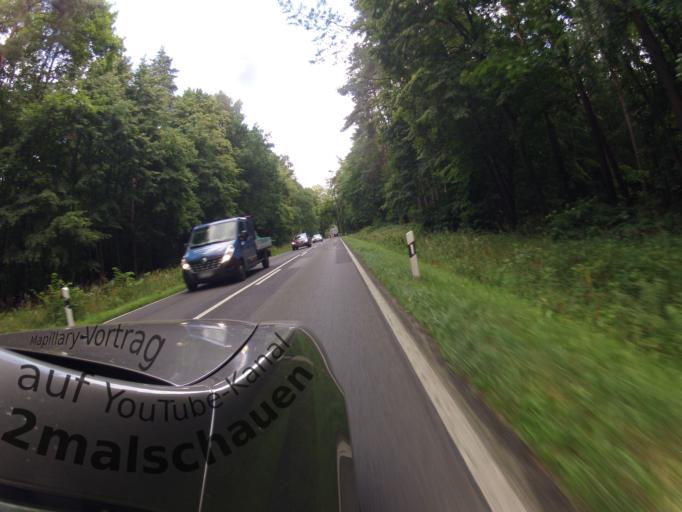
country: DE
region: Mecklenburg-Vorpommern
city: Usedom
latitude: 53.9074
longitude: 14.0278
